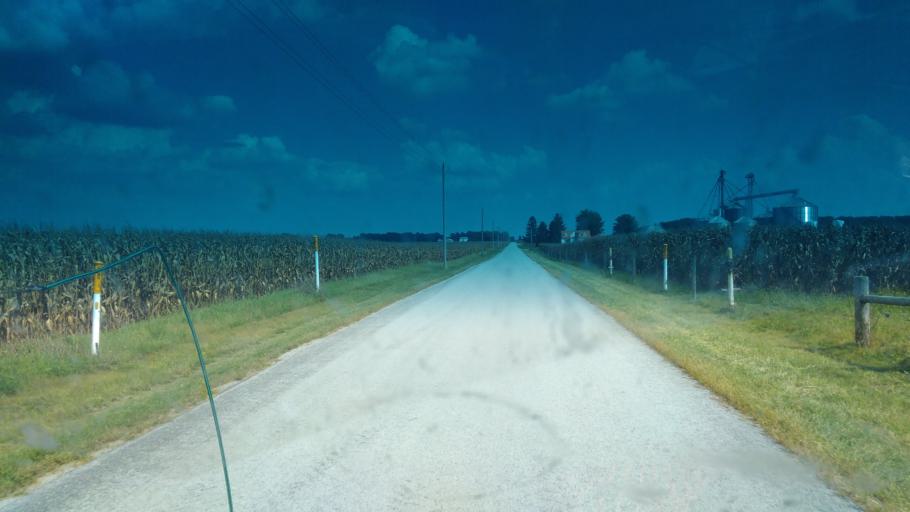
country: US
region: Ohio
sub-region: Hardin County
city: Kenton
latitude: 40.6594
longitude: -83.7147
